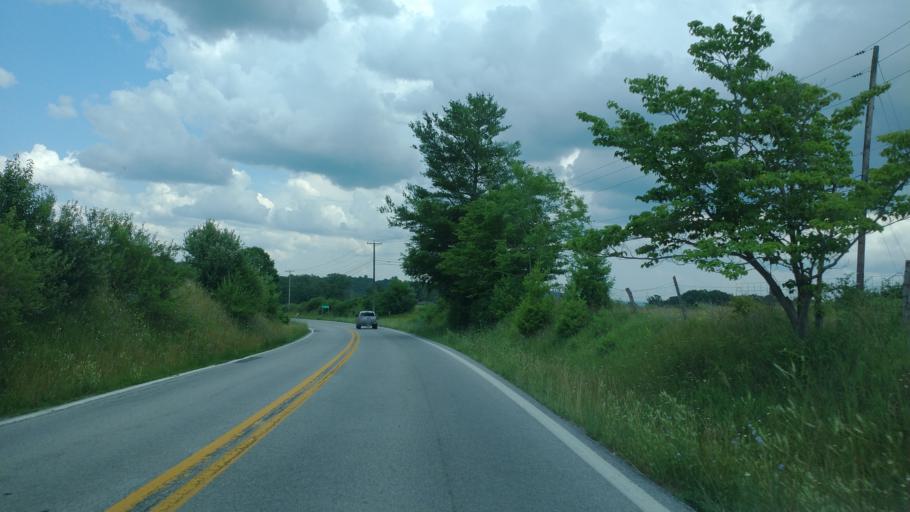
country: US
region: West Virginia
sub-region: Mercer County
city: Athens
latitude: 37.4500
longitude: -81.0064
